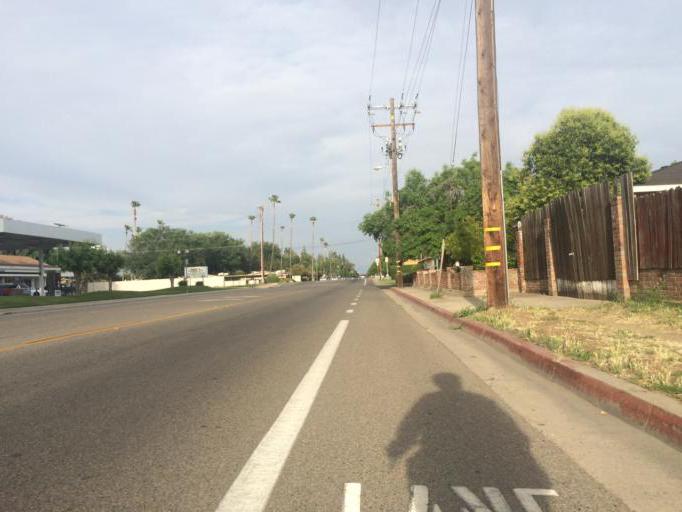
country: US
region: California
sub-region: Fresno County
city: Clovis
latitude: 36.8157
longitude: -119.7195
